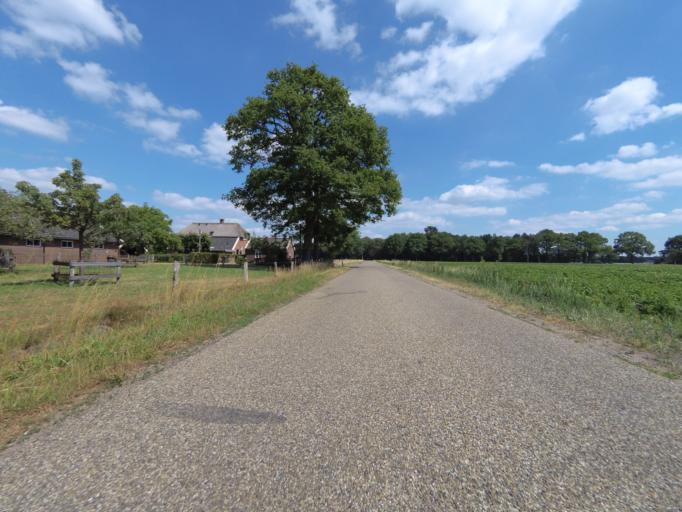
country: NL
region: Overijssel
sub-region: Gemeente Wierden
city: Wierden
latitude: 52.3463
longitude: 6.5341
